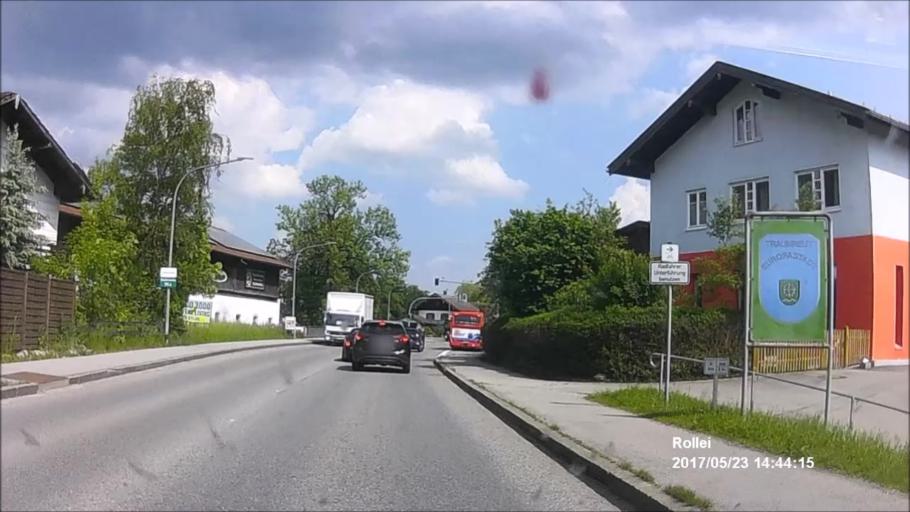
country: DE
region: Bavaria
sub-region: Upper Bavaria
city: Trostberg an der Alz
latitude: 47.9862
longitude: 12.5453
